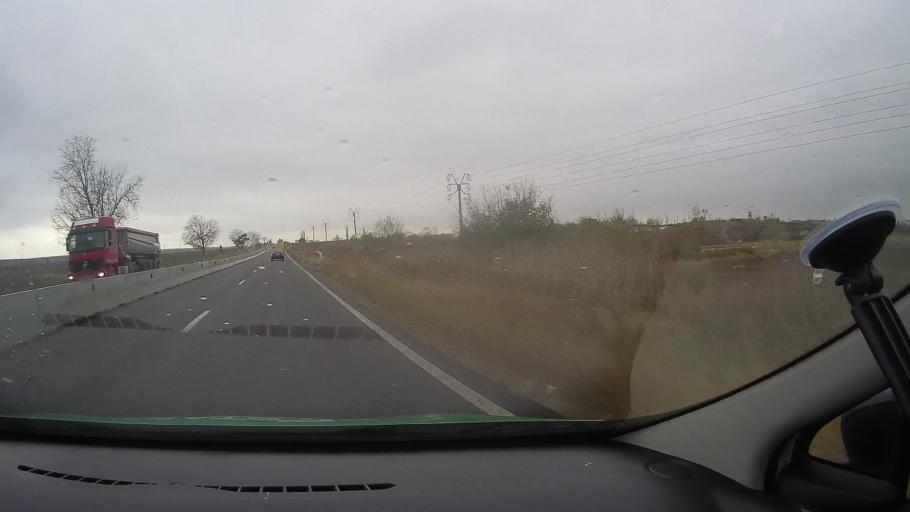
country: RO
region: Constanta
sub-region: Comuna Cumpana
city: Cumpana
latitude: 44.1663
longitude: 28.5388
